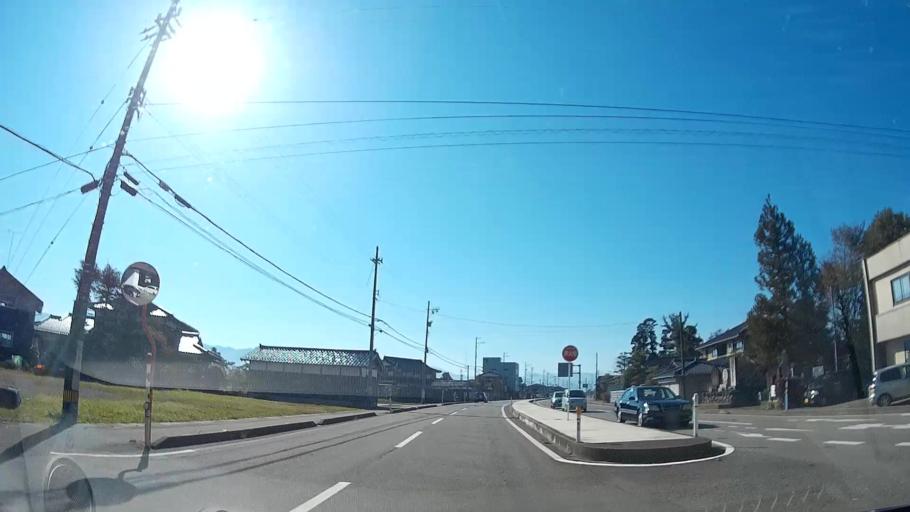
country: JP
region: Toyama
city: Nanto-shi
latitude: 36.6227
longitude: 136.9428
